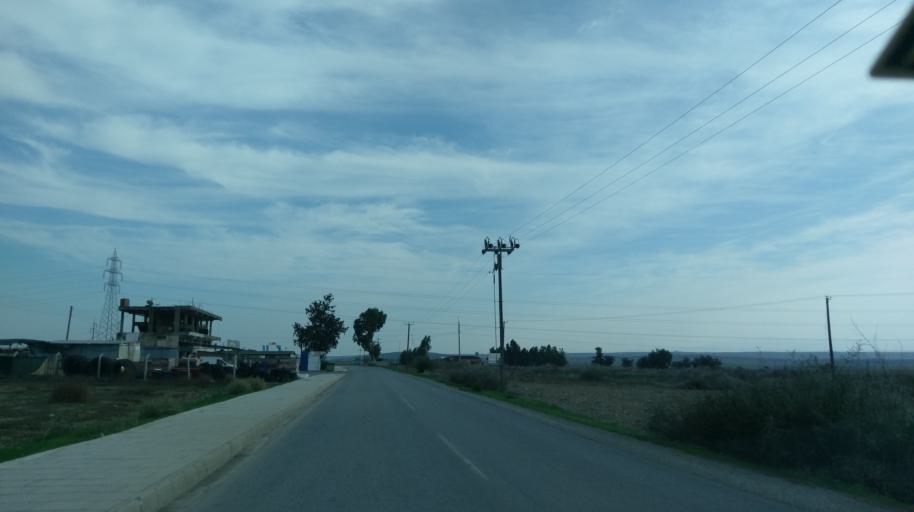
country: CY
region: Lefkosia
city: Mammari
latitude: 35.2273
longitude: 33.1714
